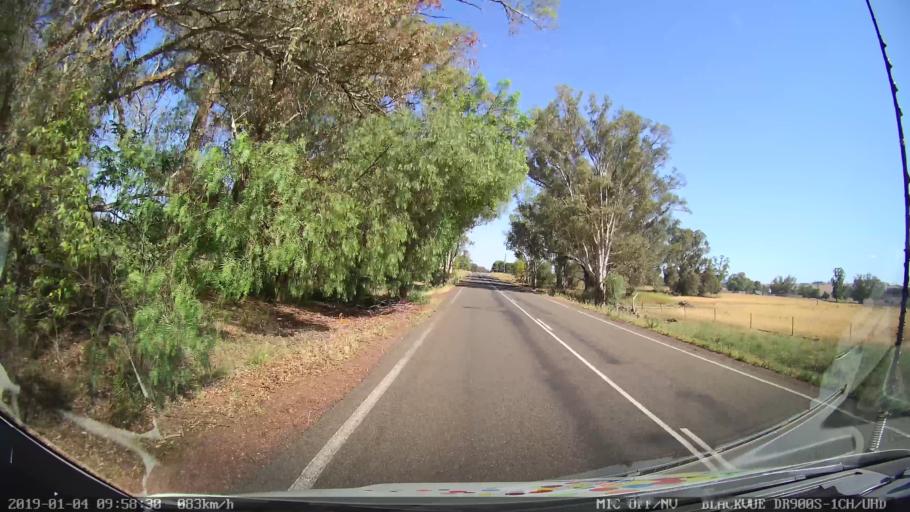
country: AU
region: New South Wales
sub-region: Cabonne
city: Canowindra
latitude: -33.5178
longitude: 148.3939
